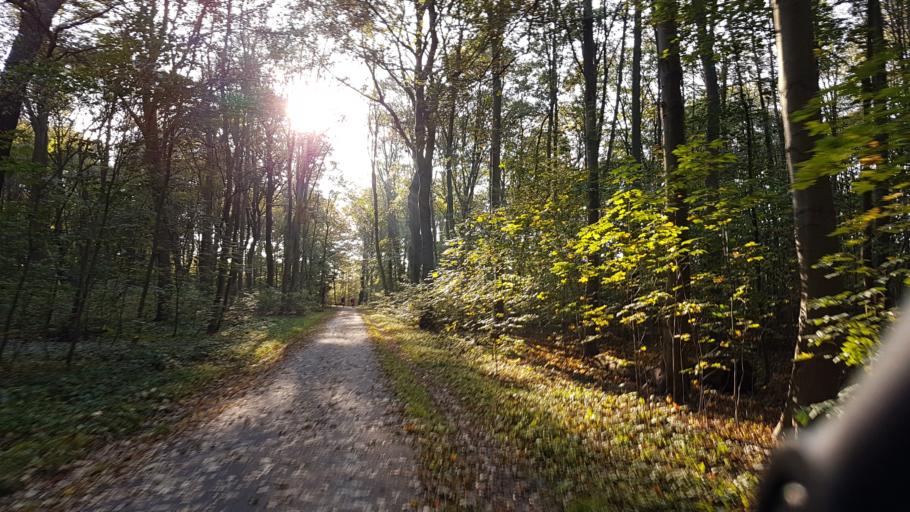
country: DE
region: Lower Saxony
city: Hannover
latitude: 52.3703
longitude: 9.7819
